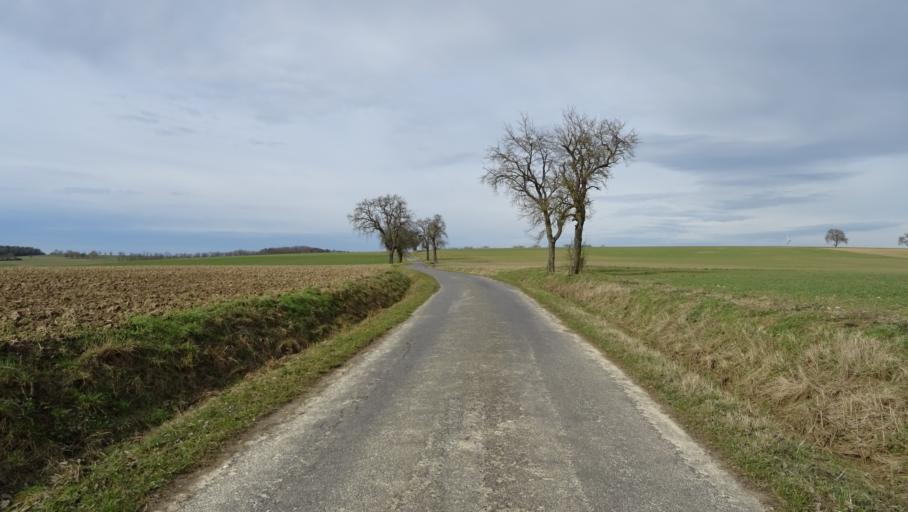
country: DE
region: Baden-Wuerttemberg
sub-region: Karlsruhe Region
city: Seckach
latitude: 49.4244
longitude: 9.2768
